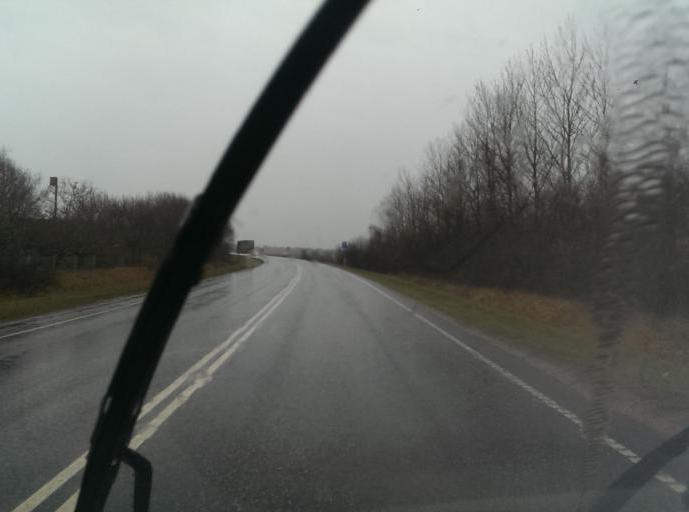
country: DK
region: Central Jutland
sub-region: Ringkobing-Skjern Kommune
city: Tarm
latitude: 55.9015
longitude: 8.5047
